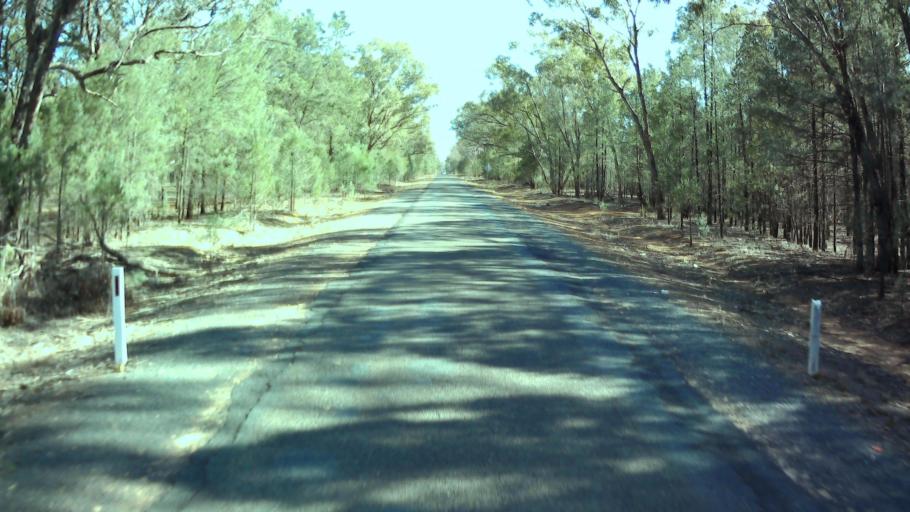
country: AU
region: New South Wales
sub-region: Weddin
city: Grenfell
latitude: -33.8117
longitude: 147.9539
